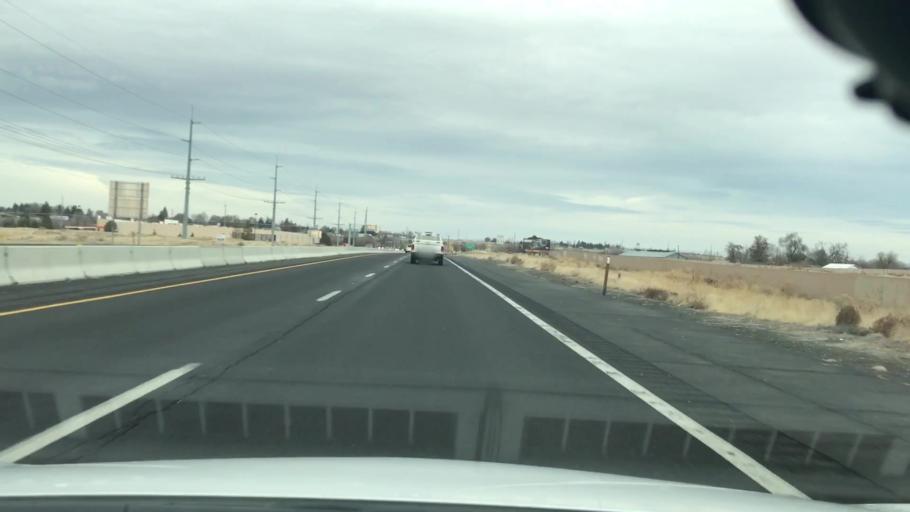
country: US
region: Washington
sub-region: Grant County
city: Moses Lake
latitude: 47.1470
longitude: -119.2874
